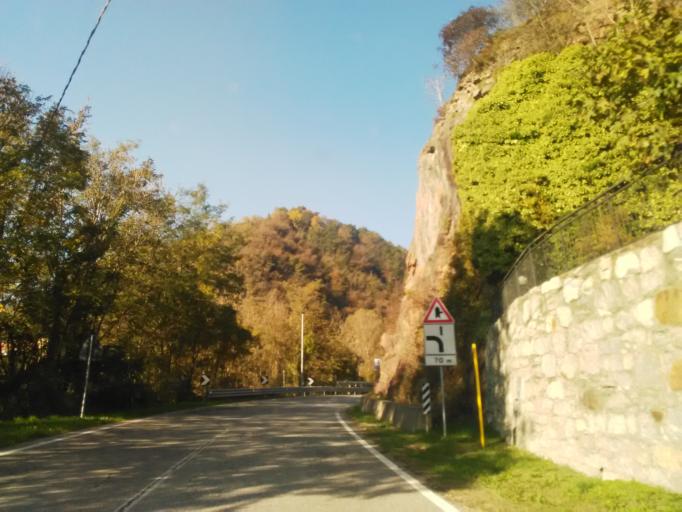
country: IT
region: Piedmont
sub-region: Provincia di Biella
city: Crevacuore
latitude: 45.6894
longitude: 8.2584
